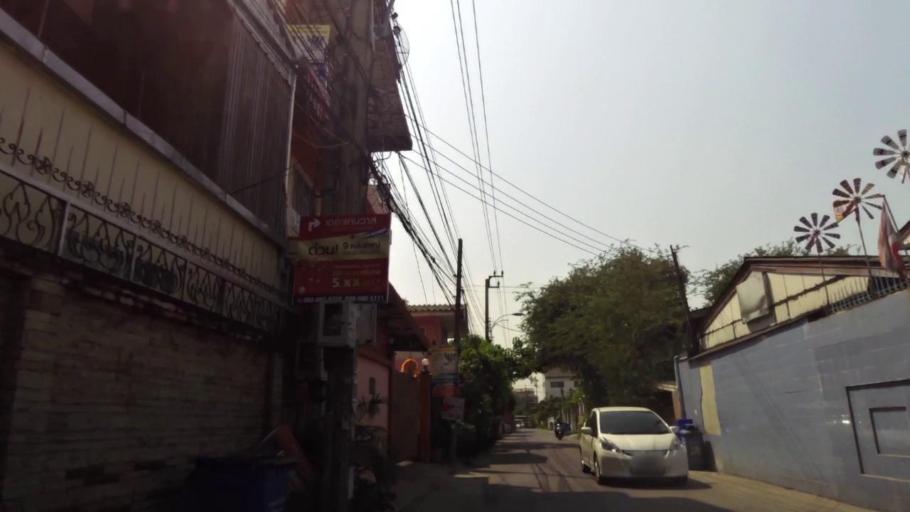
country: TH
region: Bangkok
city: Phra Khanong
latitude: 13.6558
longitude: 100.5962
